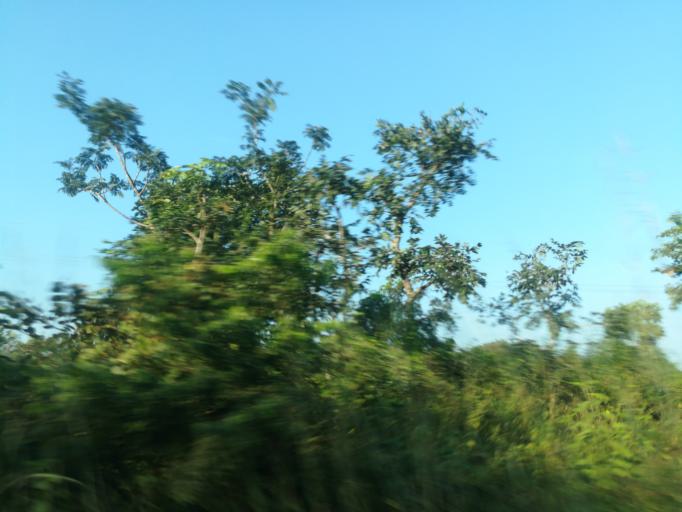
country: NG
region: Ogun
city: Abeokuta
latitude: 7.2107
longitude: 3.1998
